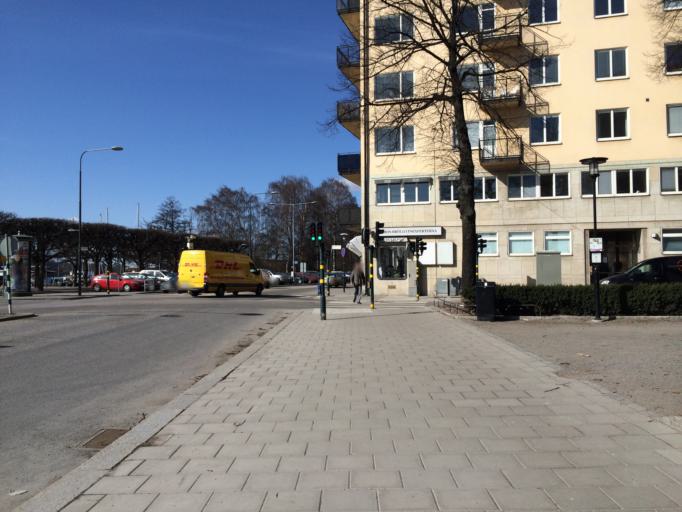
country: SE
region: Stockholm
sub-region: Stockholms Kommun
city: Stockholm
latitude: 59.3269
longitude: 18.0422
